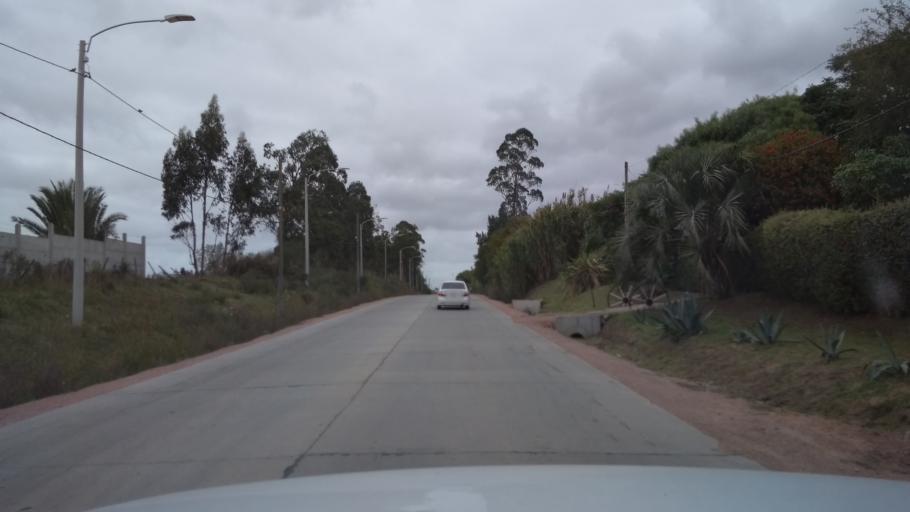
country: UY
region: Canelones
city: Toledo
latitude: -34.7937
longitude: -56.1491
